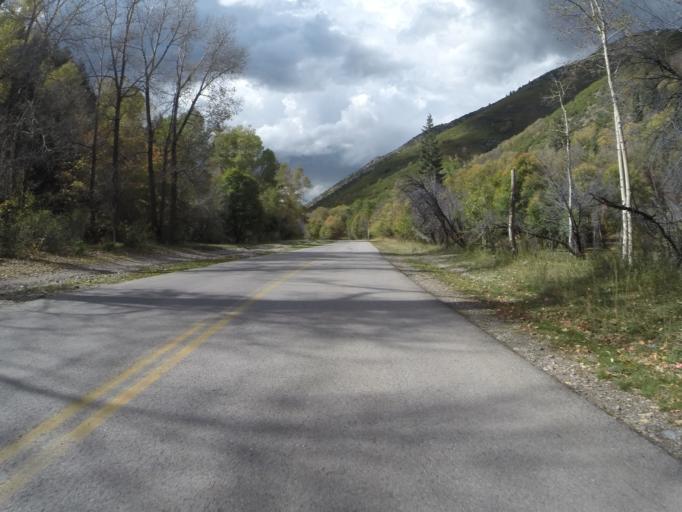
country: US
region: Utah
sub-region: Tooele County
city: Tooele
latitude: 40.4888
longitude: -112.1954
